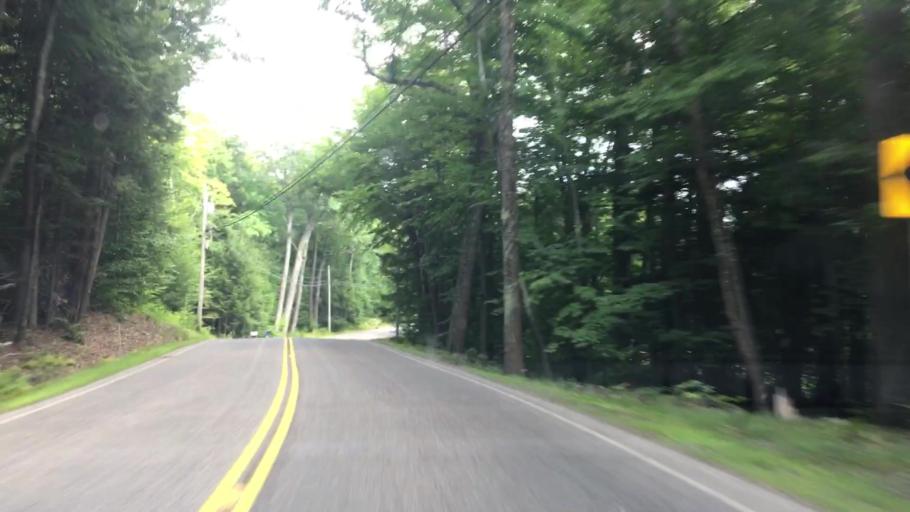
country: US
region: New Hampshire
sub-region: Belknap County
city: Sanbornton
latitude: 43.4972
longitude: -71.5927
